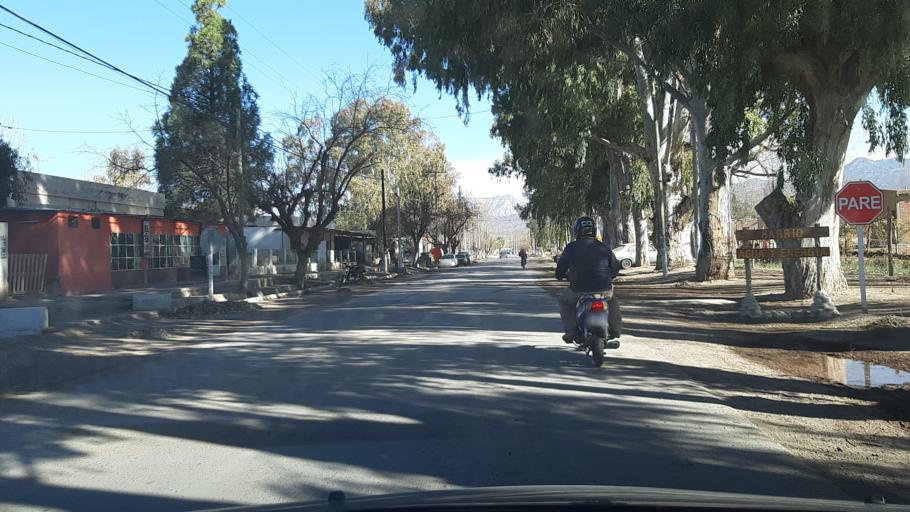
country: AR
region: San Juan
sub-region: Departamento de Zonda
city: Zonda
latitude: -31.4617
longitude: -68.7370
